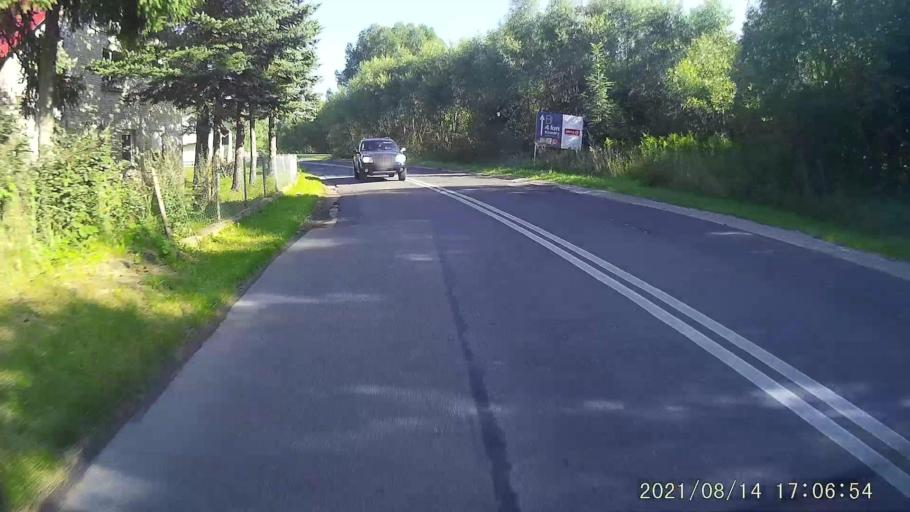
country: PL
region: Lower Silesian Voivodeship
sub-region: Powiat jeleniogorski
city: Kowary
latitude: 50.8134
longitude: 15.8099
